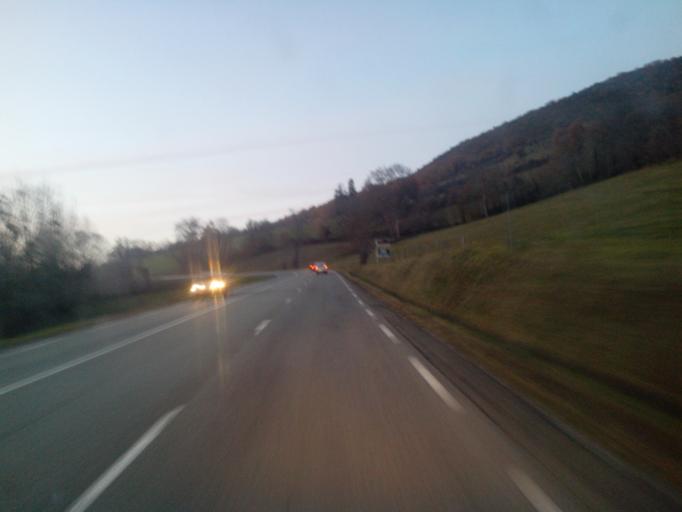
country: FR
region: Midi-Pyrenees
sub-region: Departement de l'Ariege
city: Foix
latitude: 42.9706
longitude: 1.5857
